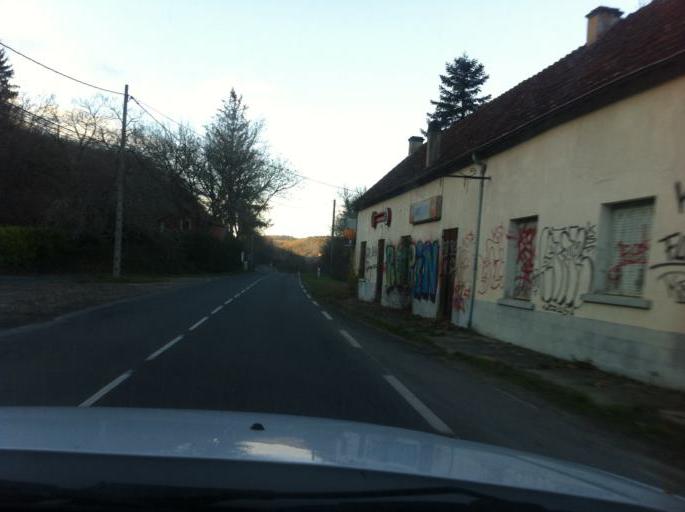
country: FR
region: Aquitaine
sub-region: Departement de la Dordogne
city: Sarlat-la-Caneda
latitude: 44.9113
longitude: 1.1625
